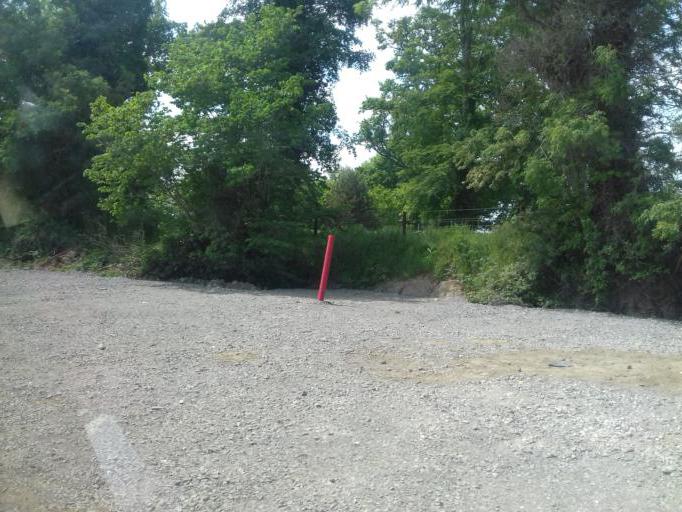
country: IE
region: Leinster
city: Donabate
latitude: 53.4917
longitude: -6.1621
